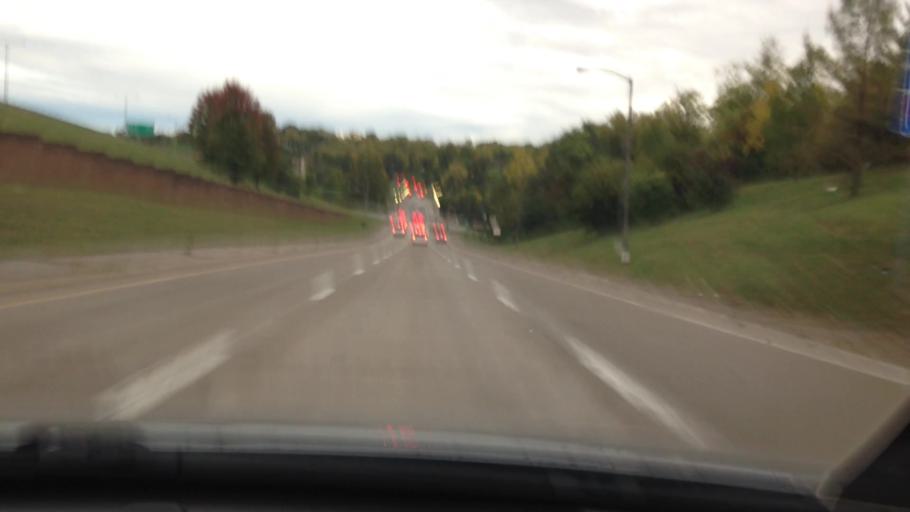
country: US
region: Kansas
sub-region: Johnson County
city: Westwood
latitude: 39.0455
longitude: -94.5619
